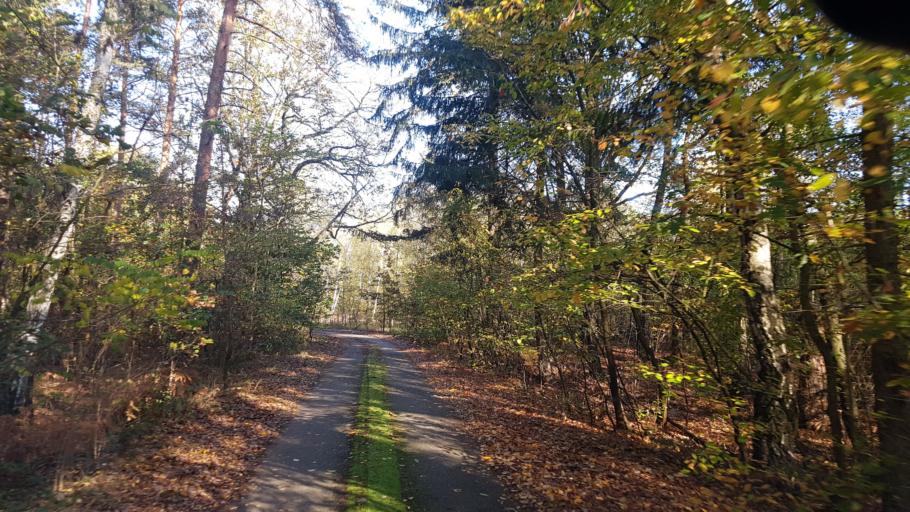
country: DE
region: Brandenburg
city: Hohenleipisch
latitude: 51.5437
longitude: 13.5349
